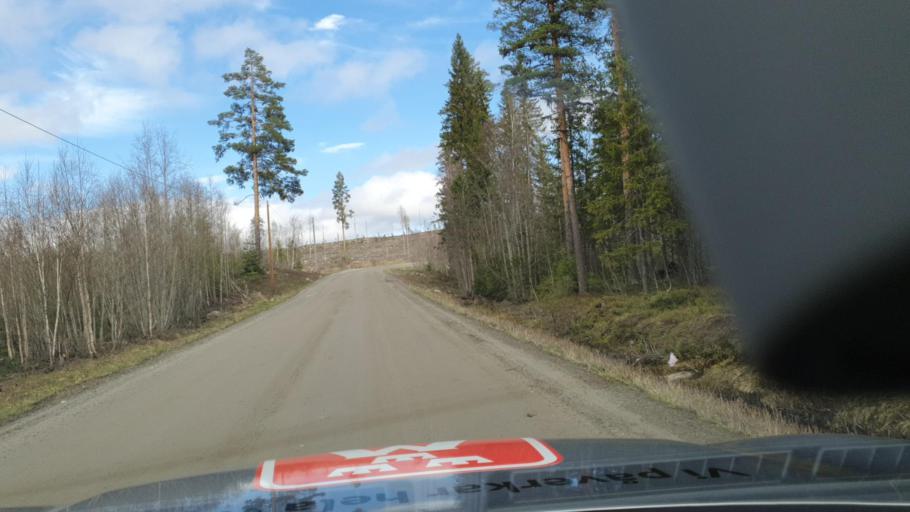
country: SE
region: Vaesterbotten
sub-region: Bjurholms Kommun
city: Bjurholm
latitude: 63.7043
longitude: 18.9027
